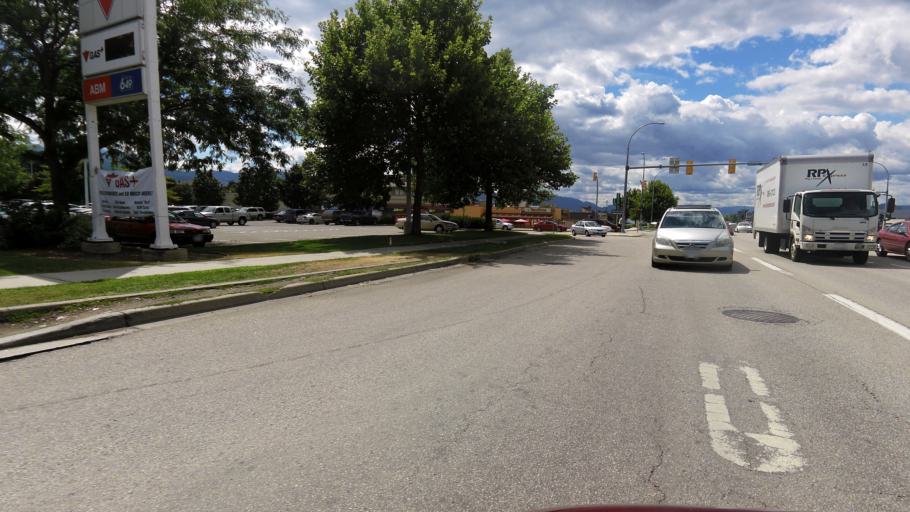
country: CA
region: British Columbia
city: Kelowna
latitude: 49.8846
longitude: -119.4283
